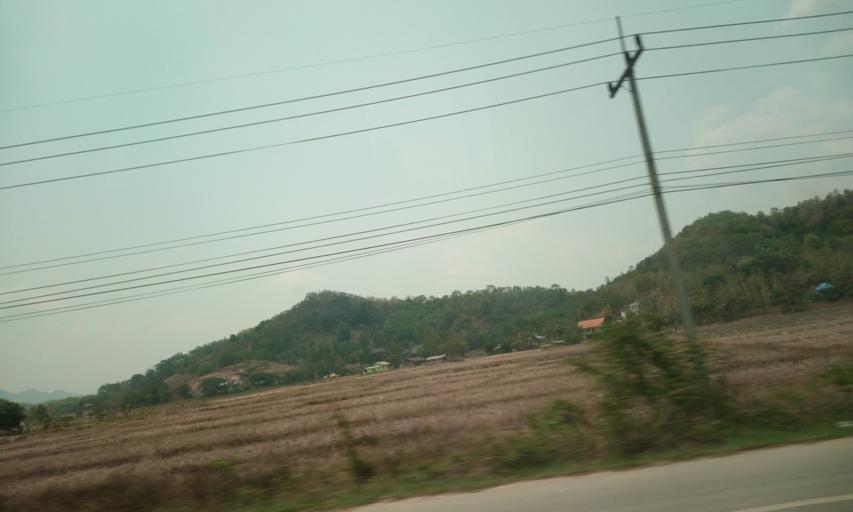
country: TH
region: Chiang Rai
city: Thoeng
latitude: 19.6900
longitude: 100.1463
